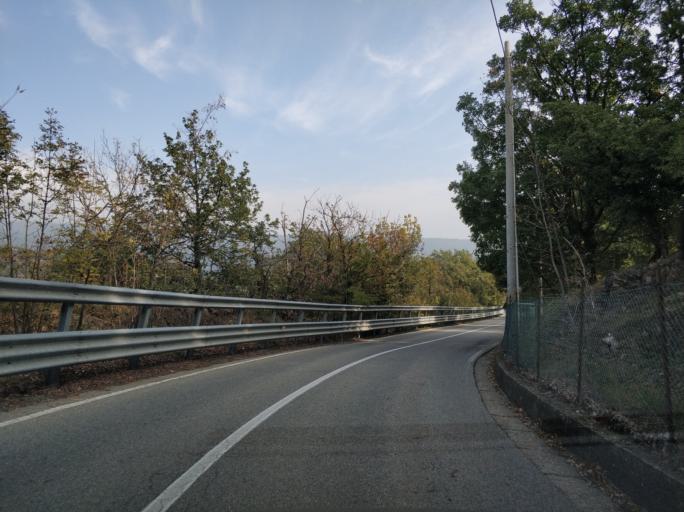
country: IT
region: Piedmont
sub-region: Provincia di Torino
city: Ivrea
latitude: 45.4834
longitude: 7.8839
